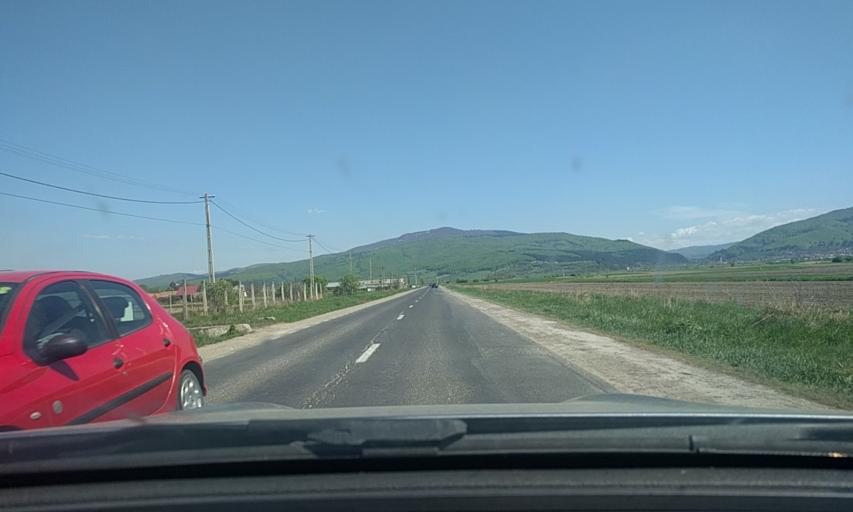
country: RO
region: Brasov
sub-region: Comuna Prejmer
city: Prejmer
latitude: 45.7129
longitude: 25.8084
